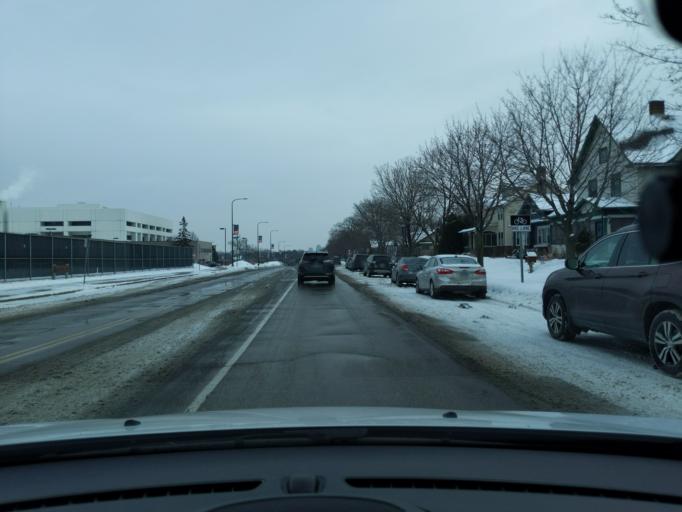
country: US
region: Minnesota
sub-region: Ramsey County
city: Falcon Heights
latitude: 44.9486
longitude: -93.1505
